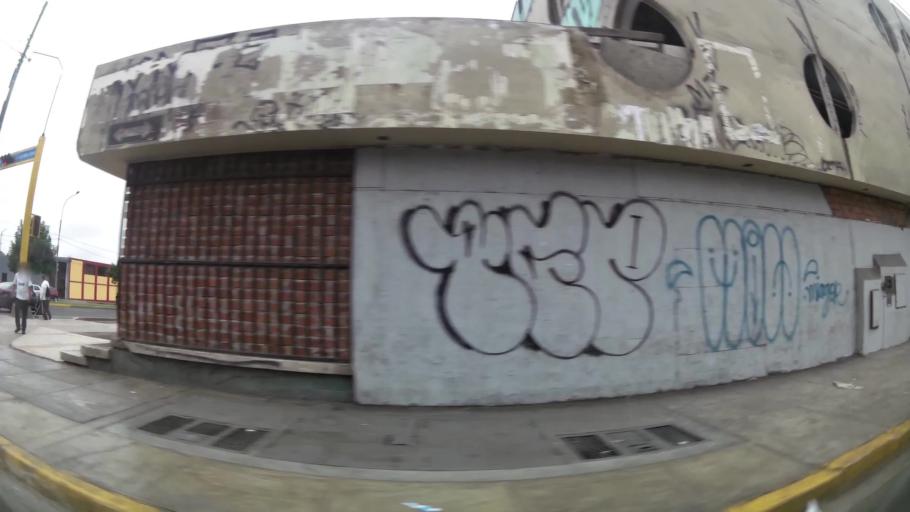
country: PE
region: Lima
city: Lima
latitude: -12.0563
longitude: -77.0616
